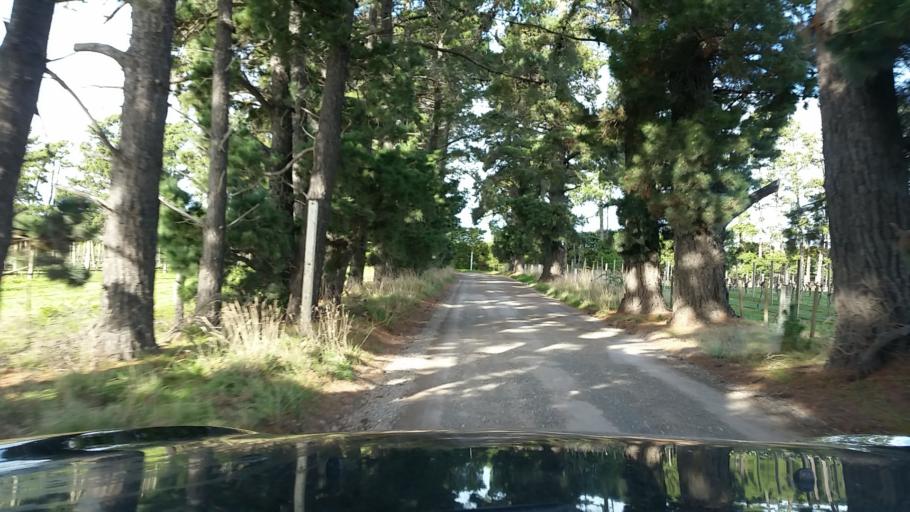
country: NZ
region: Marlborough
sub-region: Marlborough District
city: Blenheim
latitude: -41.6292
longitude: 174.1027
